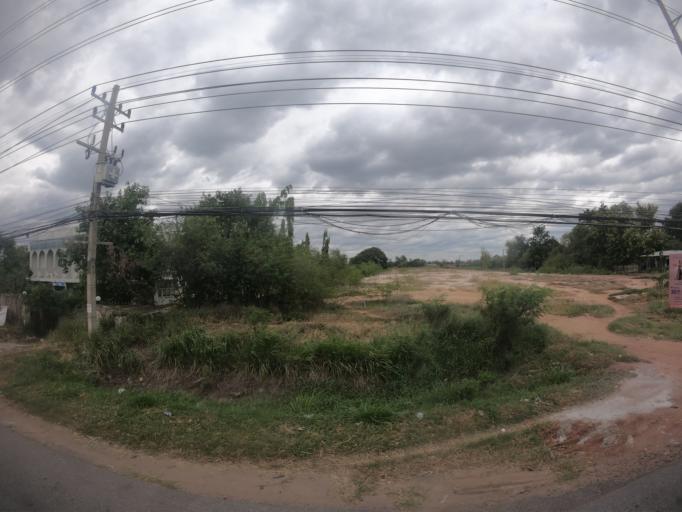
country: TH
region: Nakhon Ratchasima
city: Nakhon Ratchasima
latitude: 14.9442
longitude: 102.1289
